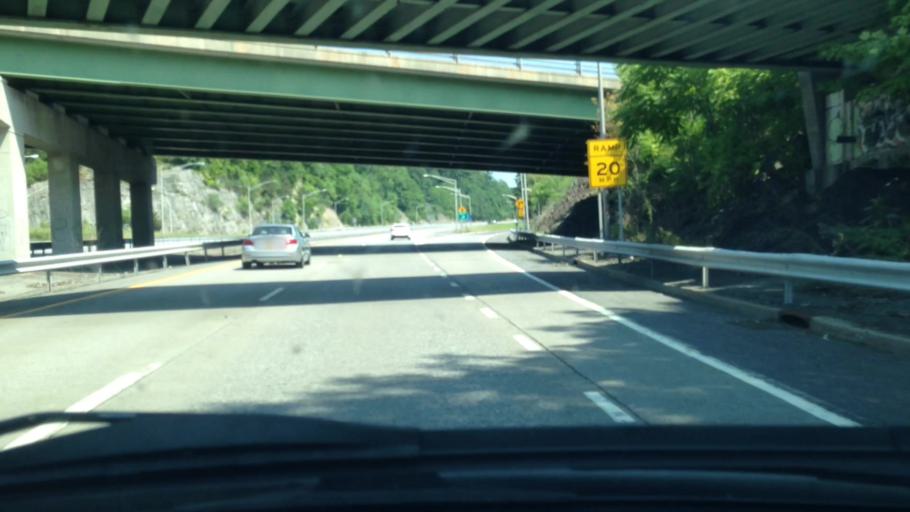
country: US
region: New York
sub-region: Ulster County
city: Kingston
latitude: 41.9264
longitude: -73.9858
